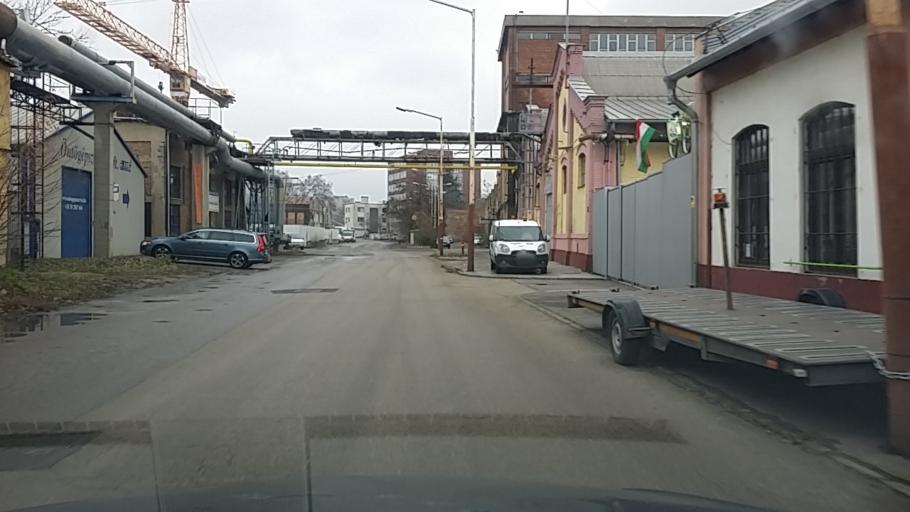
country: HU
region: Budapest
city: Budapest XXI. keruelet
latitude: 47.4268
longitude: 19.0596
